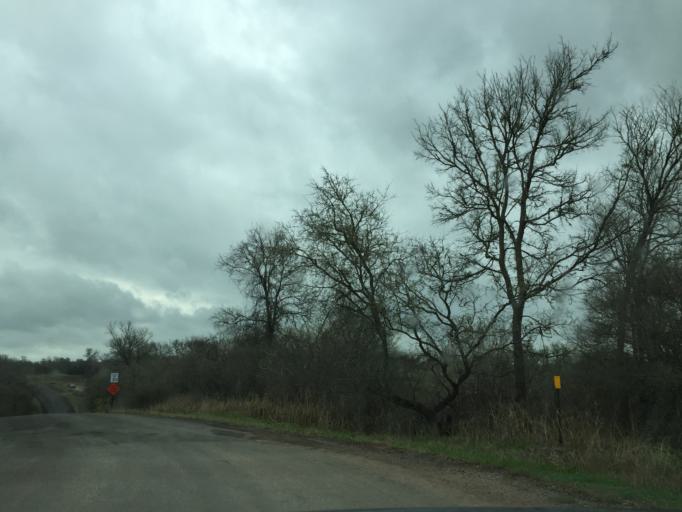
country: US
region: Texas
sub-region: Bastrop County
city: Bastrop
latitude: 30.0815
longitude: -97.3176
